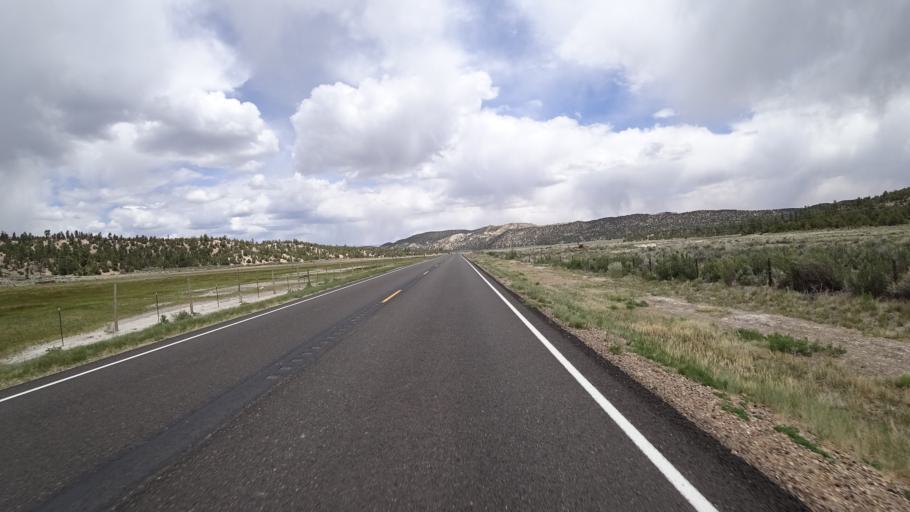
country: US
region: Utah
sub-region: Garfield County
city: Panguitch
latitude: 37.6874
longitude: -111.8058
